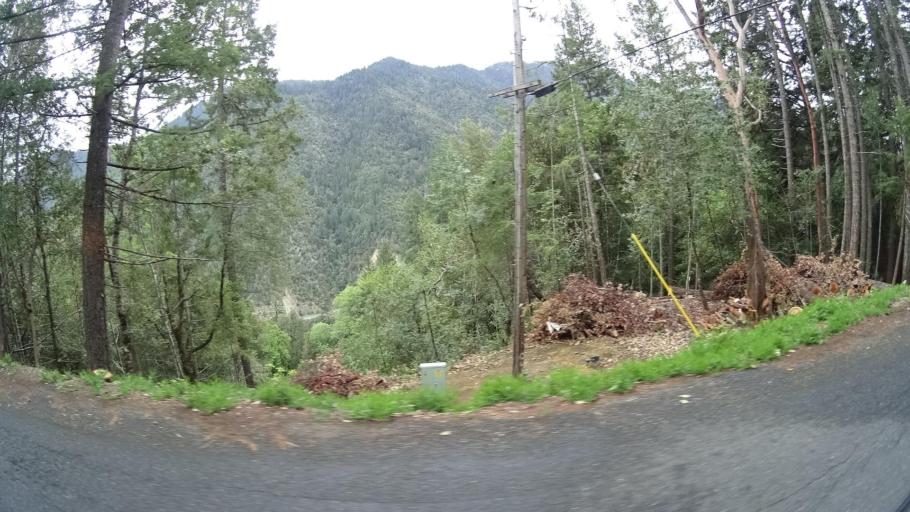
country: US
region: California
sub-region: Humboldt County
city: Willow Creek
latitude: 41.3571
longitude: -123.5086
